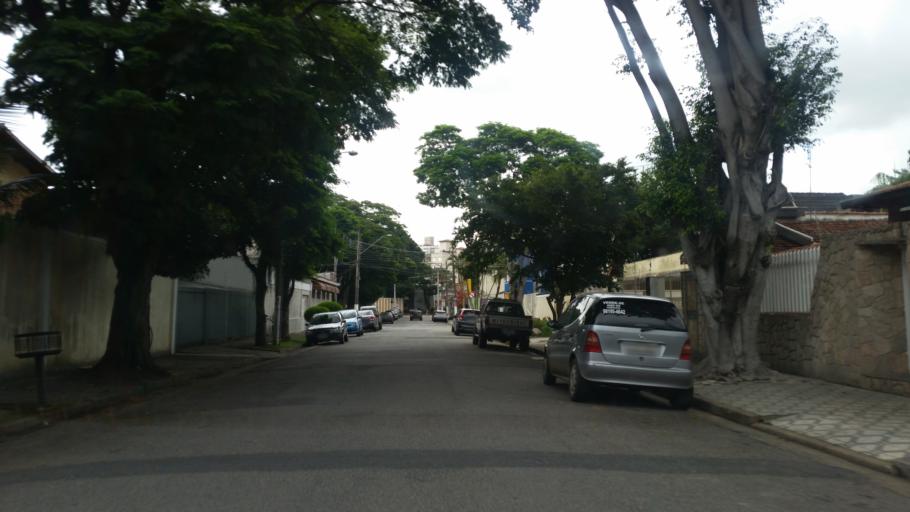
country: BR
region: Sao Paulo
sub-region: Taubate
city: Taubate
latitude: -23.0353
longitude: -45.5736
